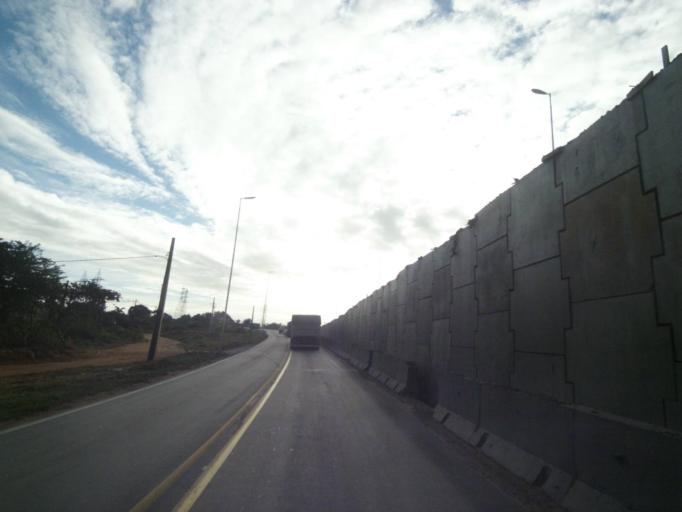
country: BR
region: Parana
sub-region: Paranagua
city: Paranagua
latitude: -25.5553
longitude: -48.5637
